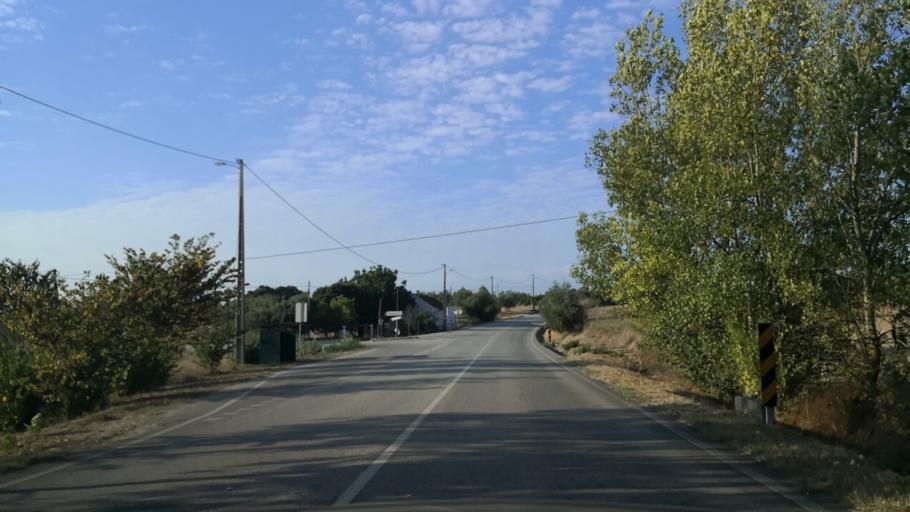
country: PT
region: Santarem
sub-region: Alcanena
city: Alcanena
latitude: 39.4005
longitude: -8.6422
